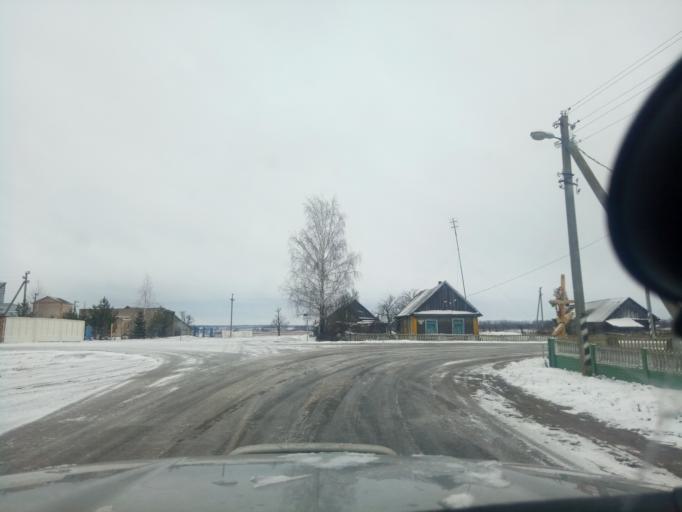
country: BY
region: Minsk
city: Klyetsk
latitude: 53.0510
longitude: 26.7438
